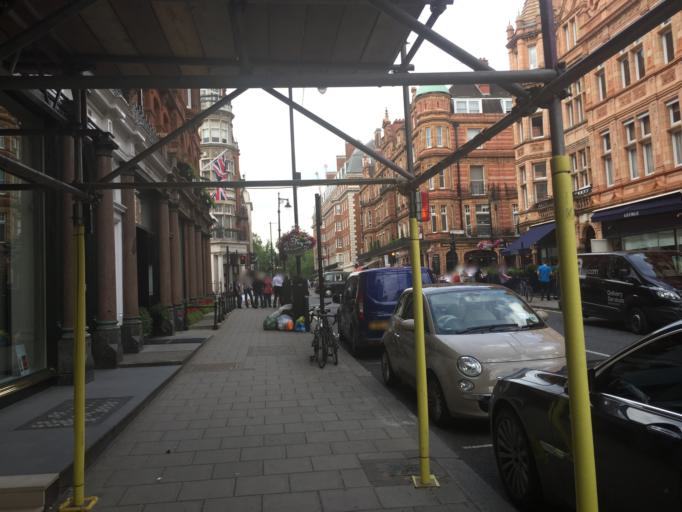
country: GB
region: England
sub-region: Greater London
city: London
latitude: 51.5091
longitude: -0.1515
